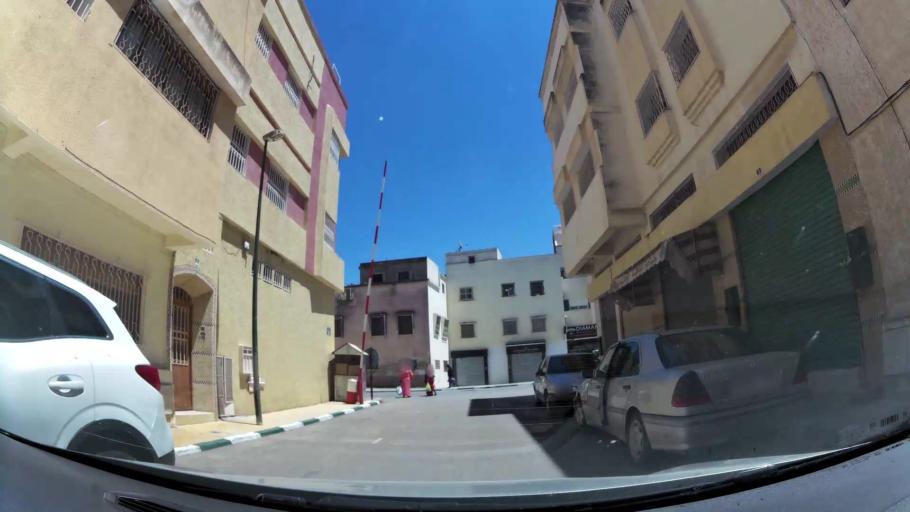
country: MA
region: Fes-Boulemane
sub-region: Fes
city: Fes
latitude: 34.0261
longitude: -5.0091
